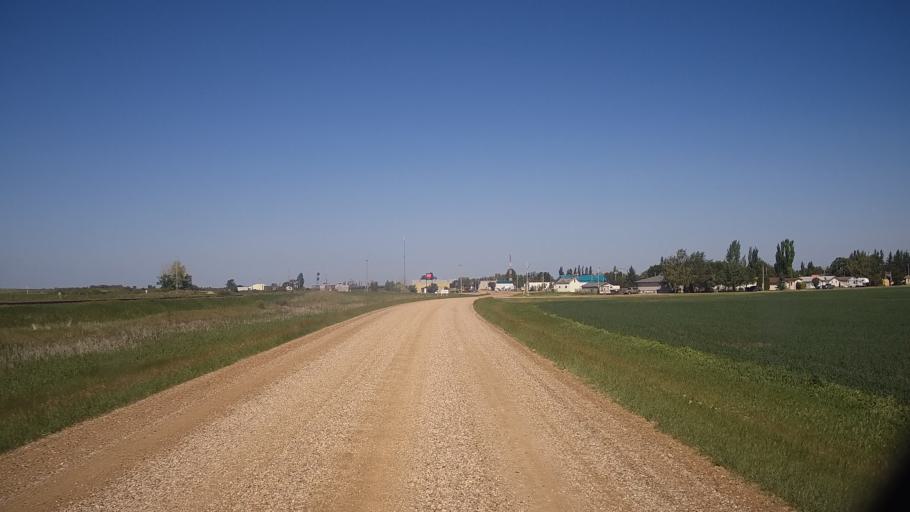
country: CA
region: Saskatchewan
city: Watrous
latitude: 51.8898
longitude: -106.0479
